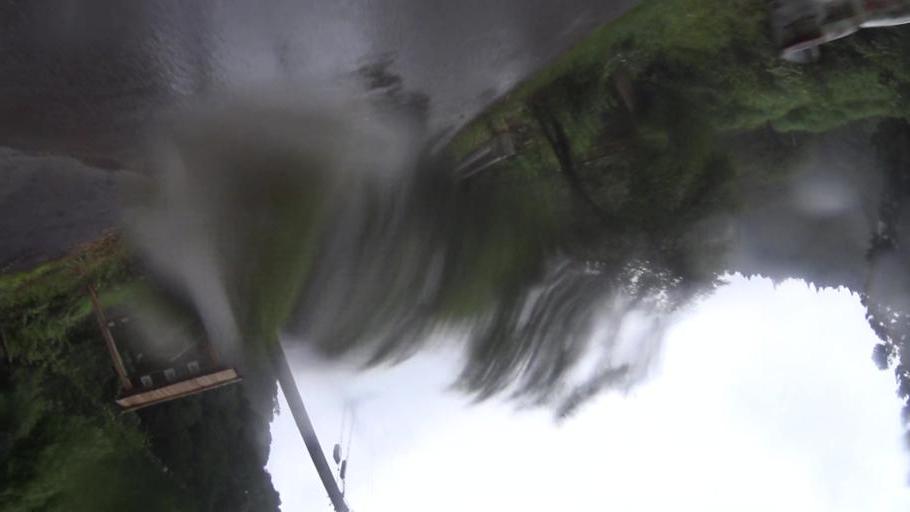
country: JP
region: Shiga Prefecture
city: Kitahama
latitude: 35.2636
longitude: 135.8245
